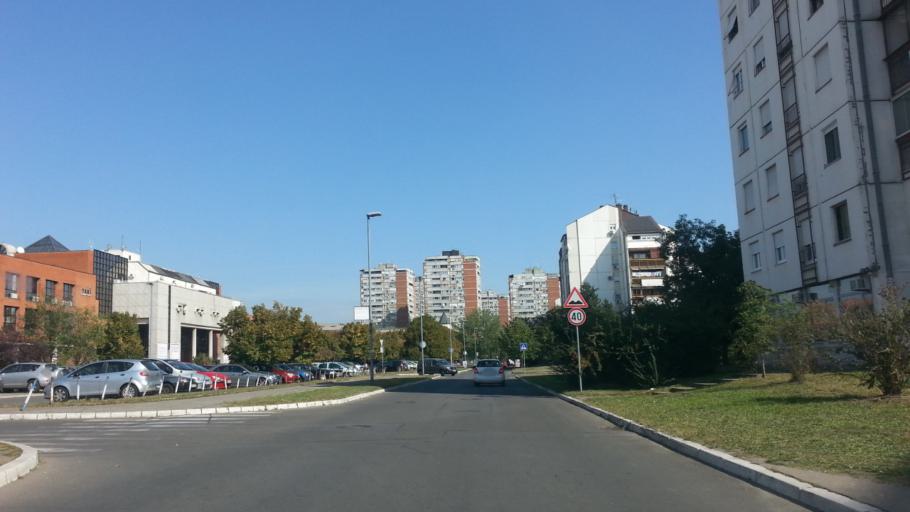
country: RS
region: Central Serbia
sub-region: Belgrade
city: Novi Beograd
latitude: 44.8007
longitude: 20.3852
